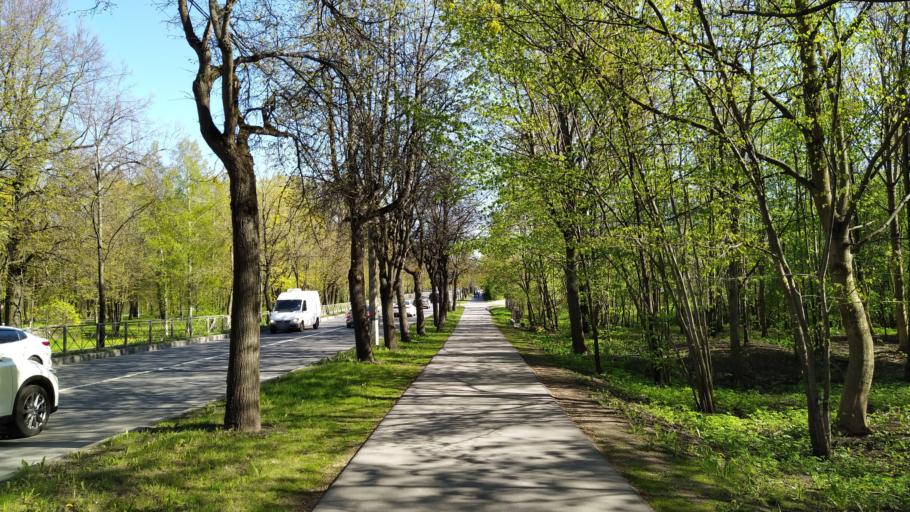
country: RU
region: St.-Petersburg
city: Pavlovsk
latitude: 59.7016
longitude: 30.4212
